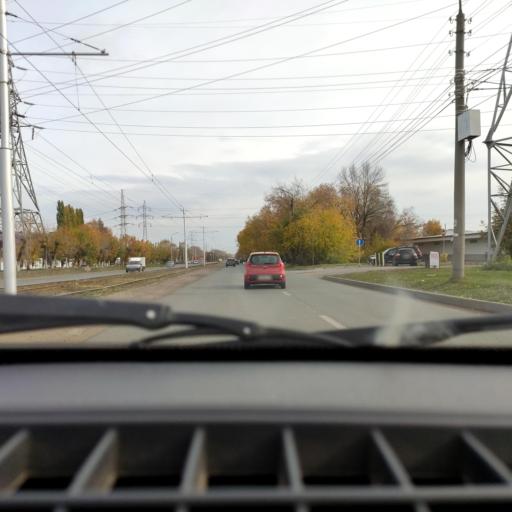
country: RU
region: Bashkortostan
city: Ufa
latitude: 54.7976
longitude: 56.0616
